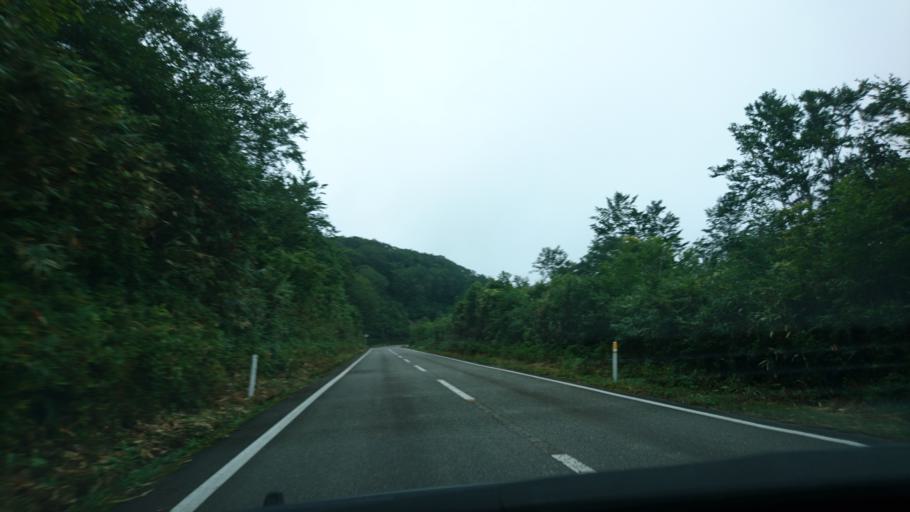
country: JP
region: Akita
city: Yuzawa
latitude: 38.9760
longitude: 140.7500
